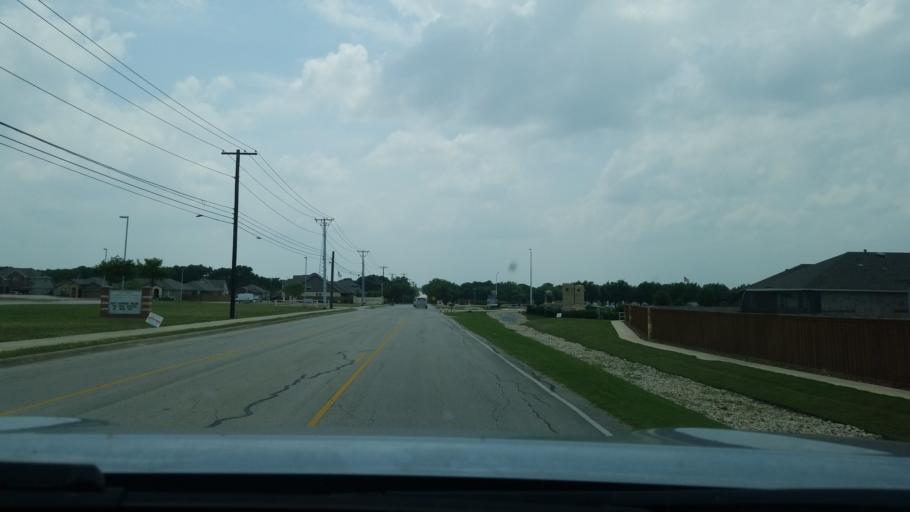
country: US
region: Texas
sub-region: Comal County
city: New Braunfels
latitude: 29.7511
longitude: -98.0717
